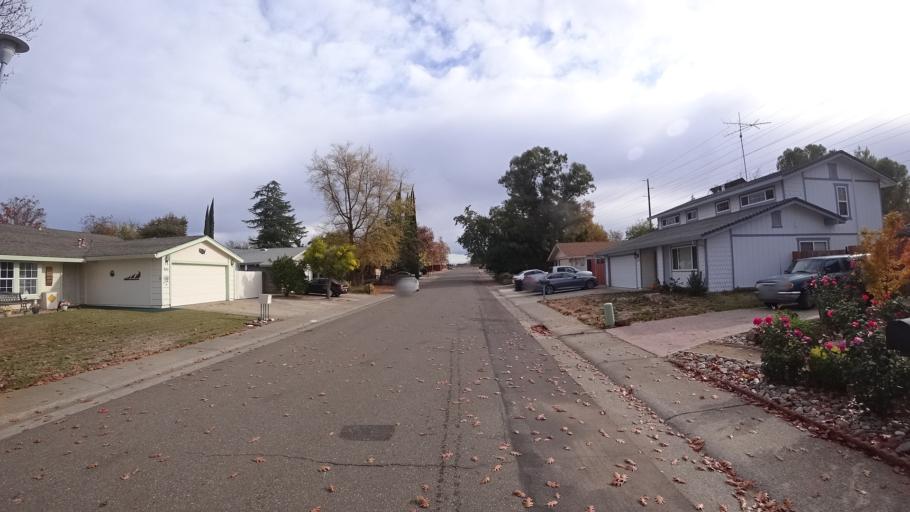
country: US
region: California
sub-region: Sacramento County
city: Citrus Heights
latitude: 38.7086
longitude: -121.2464
